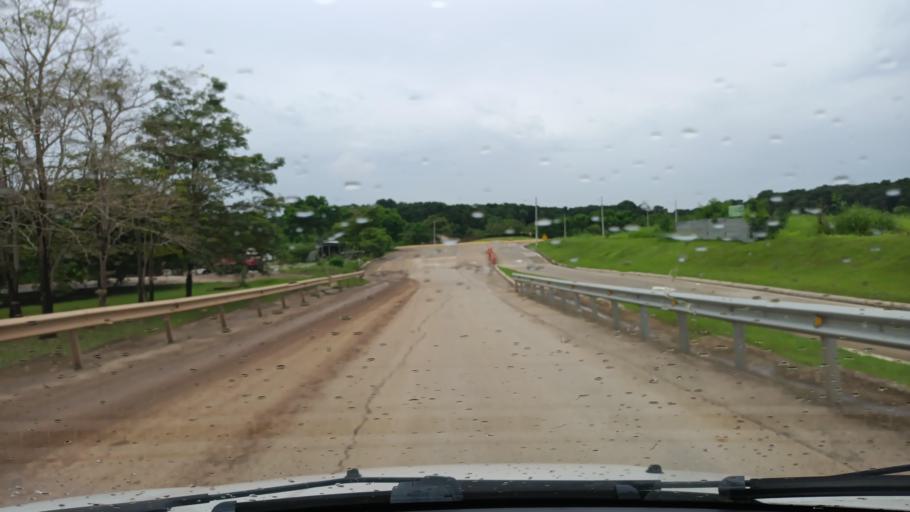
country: PA
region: Panama
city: Tocumen
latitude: 9.0392
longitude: -79.4053
